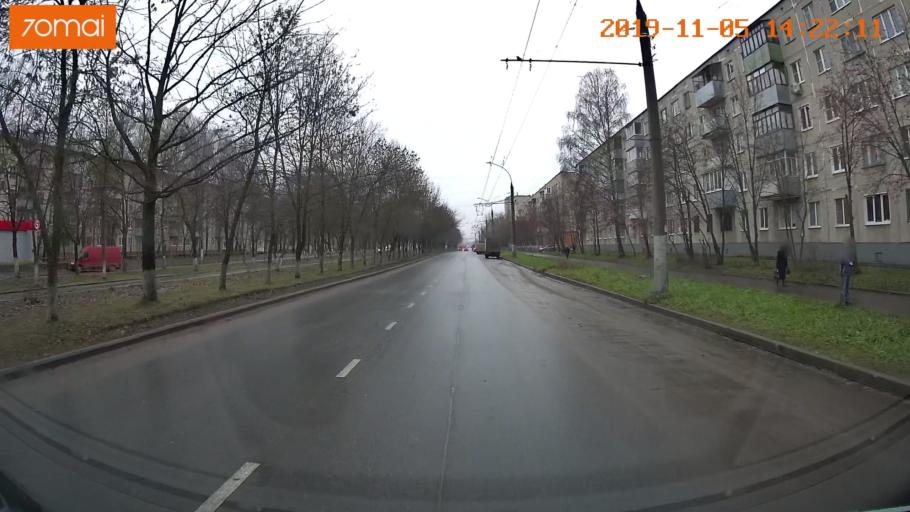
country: RU
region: Ivanovo
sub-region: Gorod Ivanovo
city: Ivanovo
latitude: 56.9621
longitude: 41.0066
